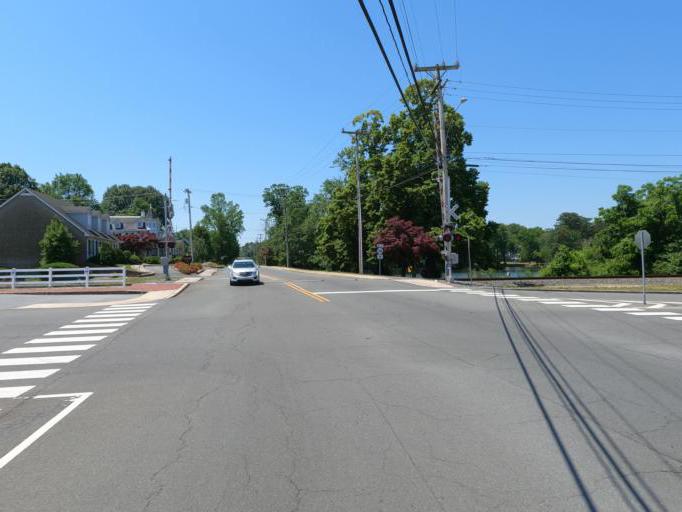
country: US
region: Delaware
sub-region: Sussex County
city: Milford
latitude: 38.9113
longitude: -75.4323
